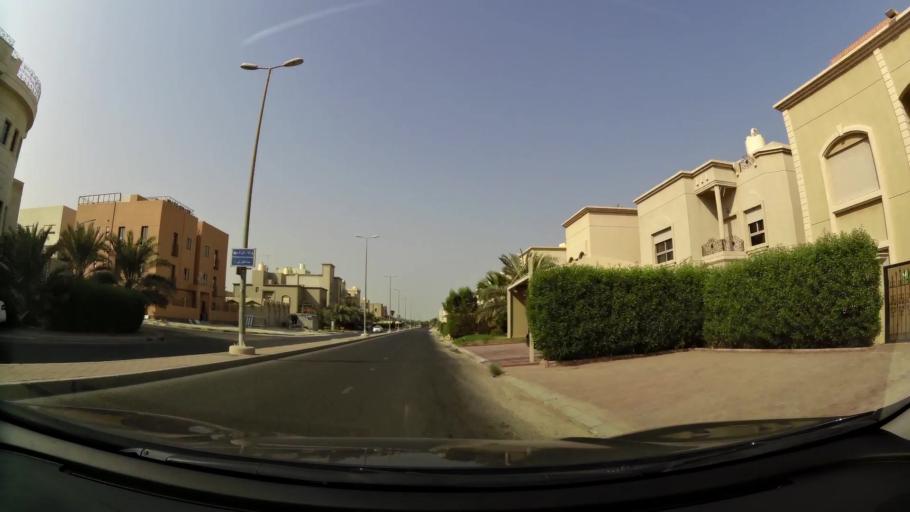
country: KW
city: Bayan
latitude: 29.2852
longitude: 48.0482
